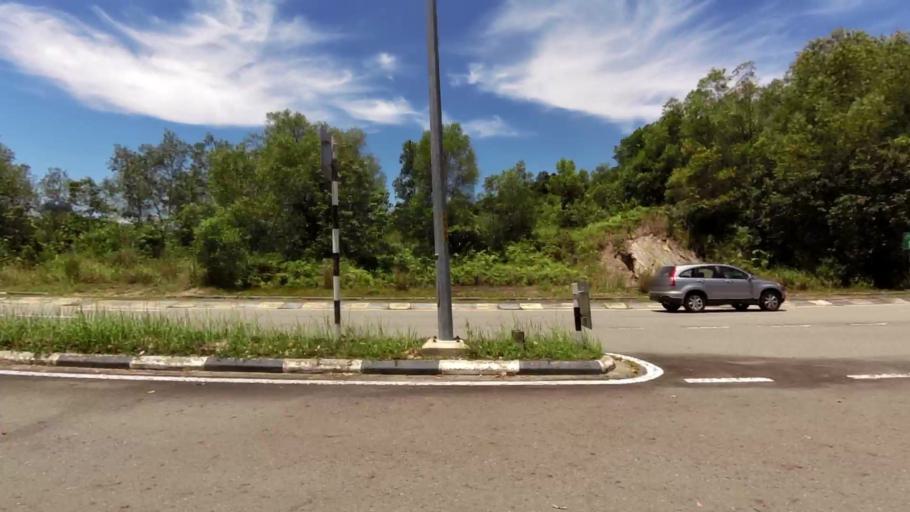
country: BN
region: Brunei and Muara
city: Bandar Seri Begawan
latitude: 4.9162
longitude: 114.9450
